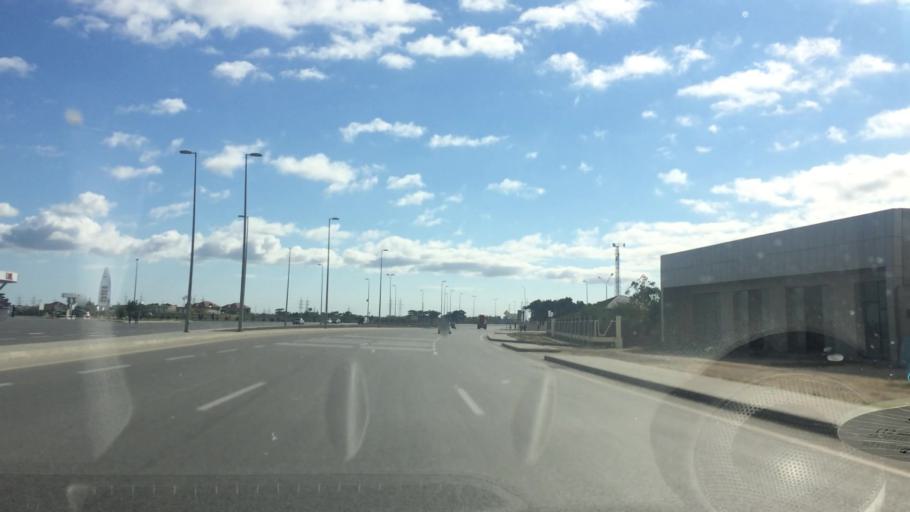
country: AZ
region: Baki
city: Qala
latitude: 40.4451
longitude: 50.1746
